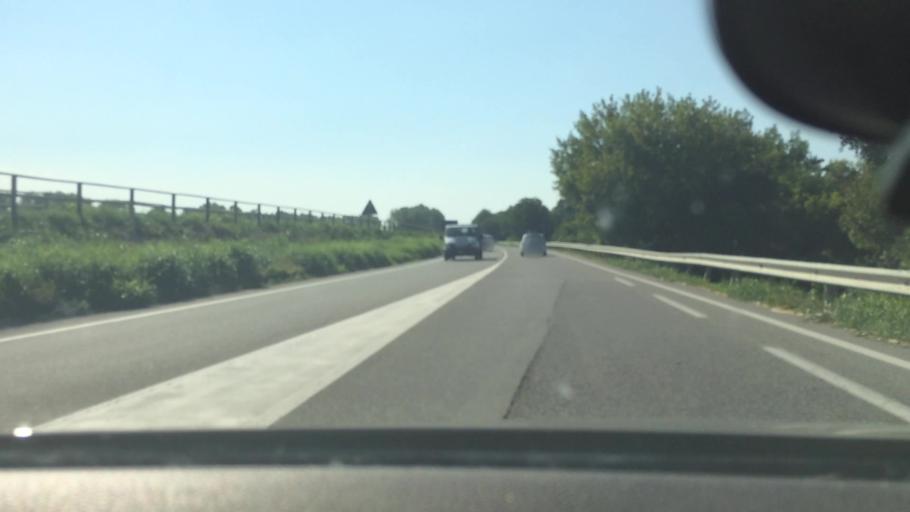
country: IT
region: Lombardy
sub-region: Provincia di Lodi
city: San Rocco al Porto
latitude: 45.0780
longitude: 9.7020
